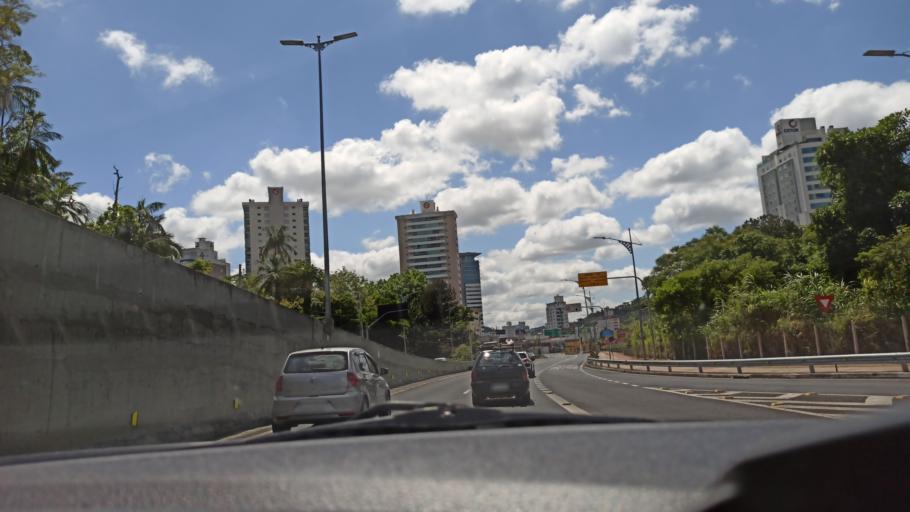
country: BR
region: Santa Catarina
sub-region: Blumenau
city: Blumenau
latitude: -26.9155
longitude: -49.0940
